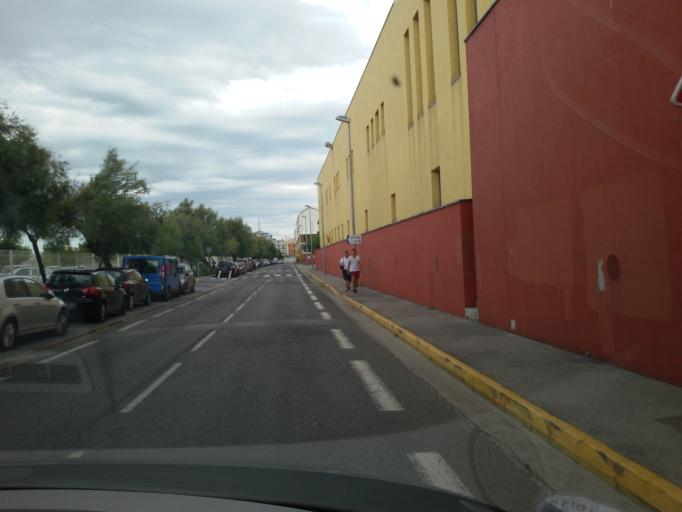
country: FR
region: Languedoc-Roussillon
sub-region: Departement de l'Herault
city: Palavas-les-Flots
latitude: 43.5241
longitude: 3.9223
